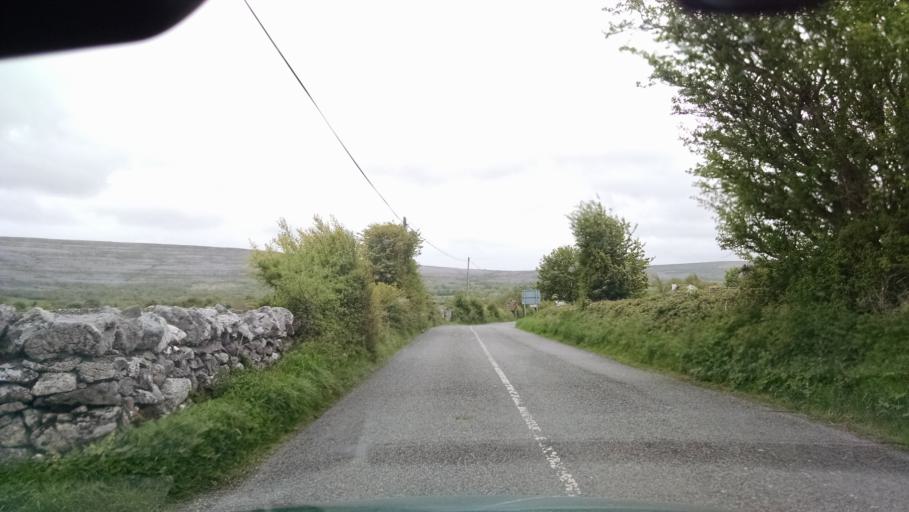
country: IE
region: Connaught
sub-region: County Galway
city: Bearna
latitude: 53.1023
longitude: -9.1594
